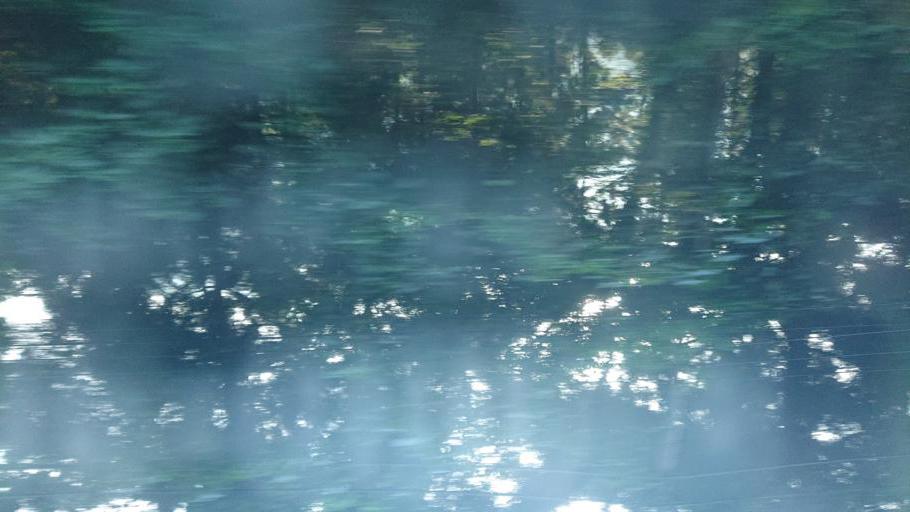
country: TW
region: Taiwan
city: Lugu
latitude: 23.4864
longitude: 120.7501
